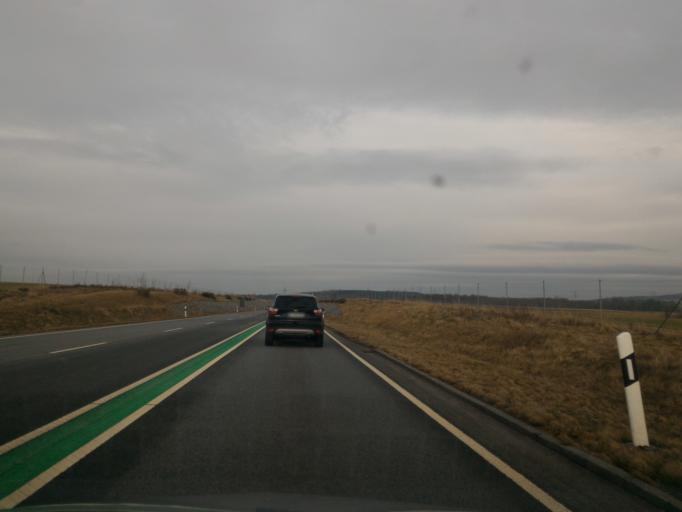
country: DE
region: Saxony
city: Niedercunnersdorf
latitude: 51.0248
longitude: 14.6853
